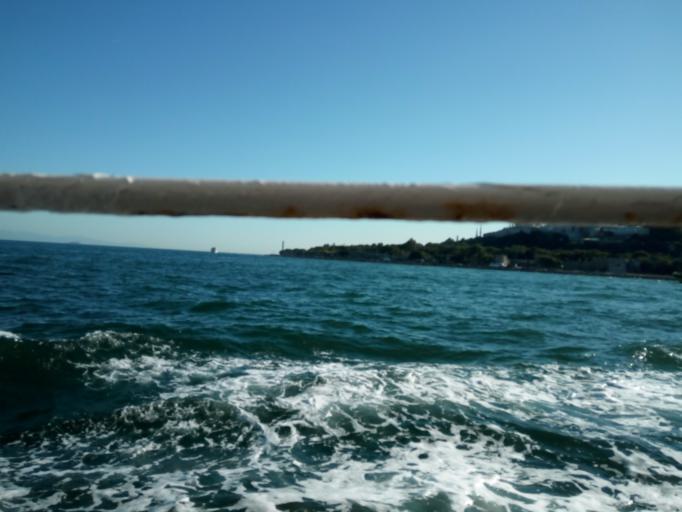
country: TR
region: Istanbul
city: Eminoenue
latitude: 41.0166
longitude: 28.9922
